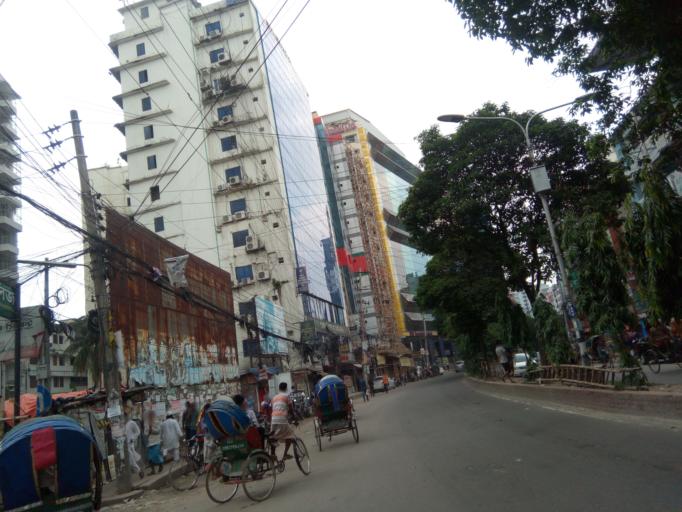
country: BD
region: Dhaka
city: Azimpur
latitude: 23.7528
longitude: 90.3843
